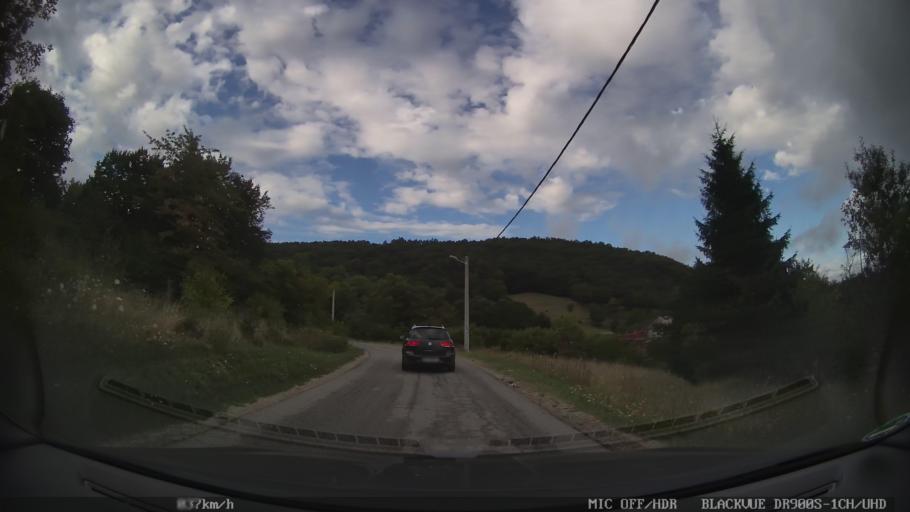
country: HR
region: Licko-Senjska
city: Jezerce
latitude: 44.9235
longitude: 15.6005
